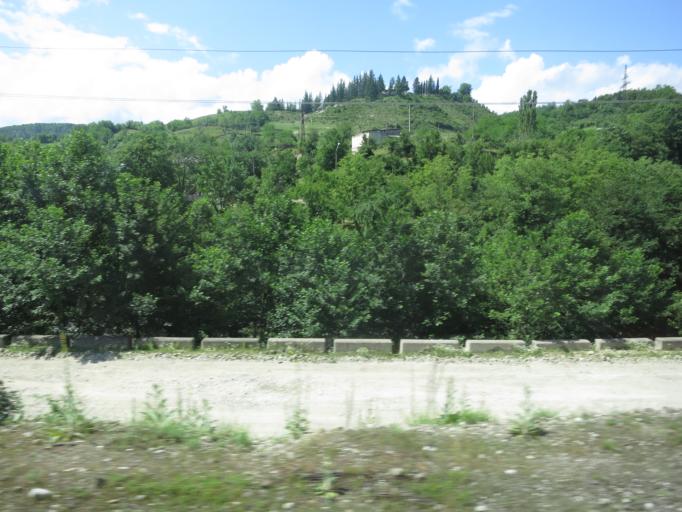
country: GE
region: Imereti
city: Kharagauli
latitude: 42.0282
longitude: 43.1961
